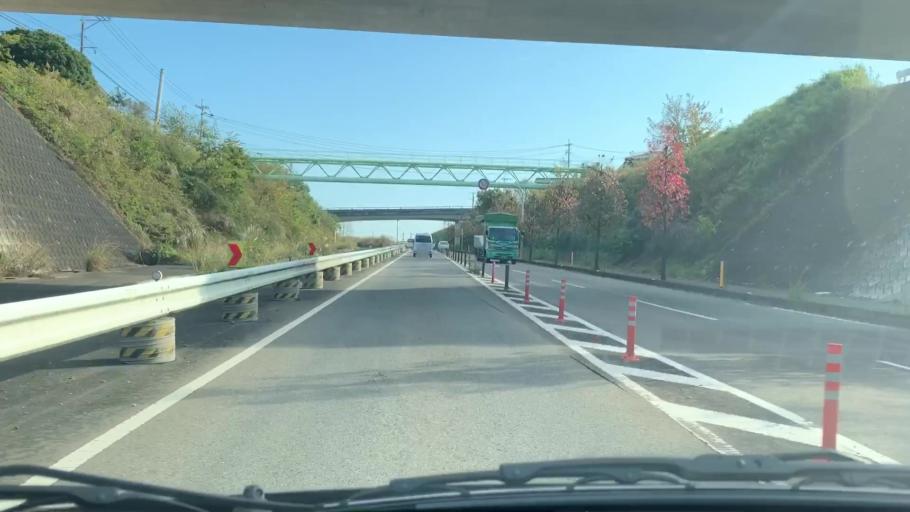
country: JP
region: Saga Prefecture
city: Kashima
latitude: 33.1020
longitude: 130.0868
